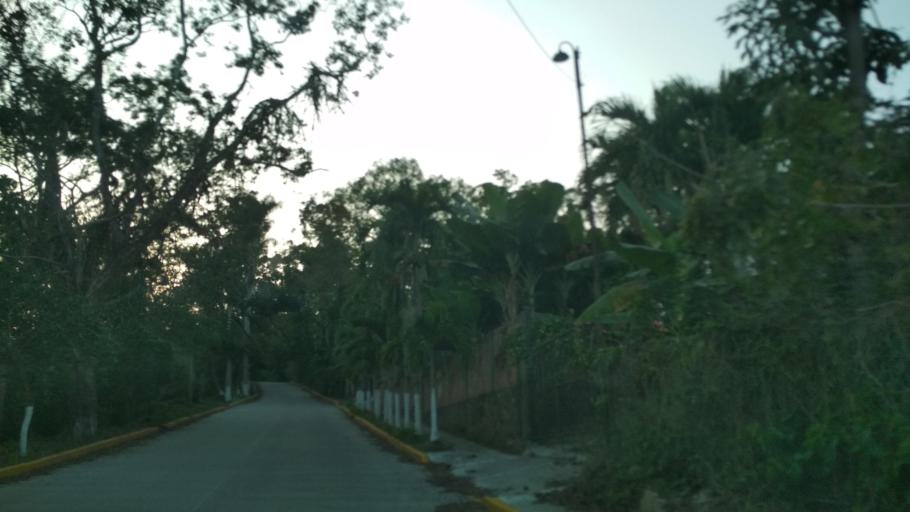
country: MX
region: Veracruz
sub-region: Poza Rica de Hidalgo
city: Arroyo del Maiz Uno
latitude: 20.4775
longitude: -97.3887
